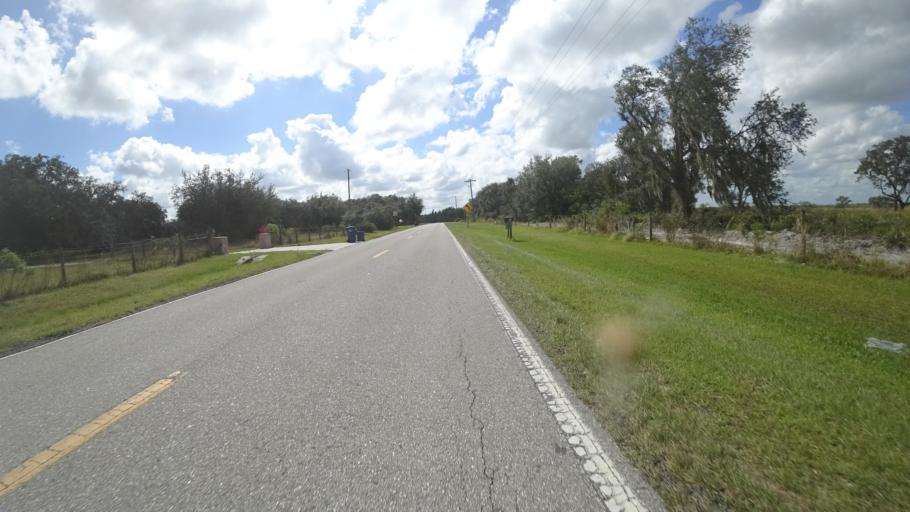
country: US
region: Florida
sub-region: Sarasota County
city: Lake Sarasota
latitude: 27.4103
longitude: -82.1334
